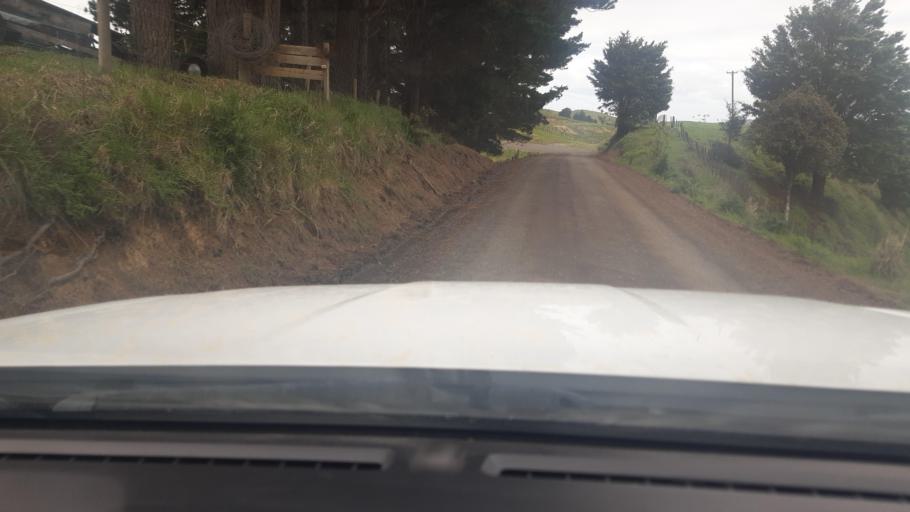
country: NZ
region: Northland
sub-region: Far North District
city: Kaitaia
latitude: -35.0778
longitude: 173.3212
